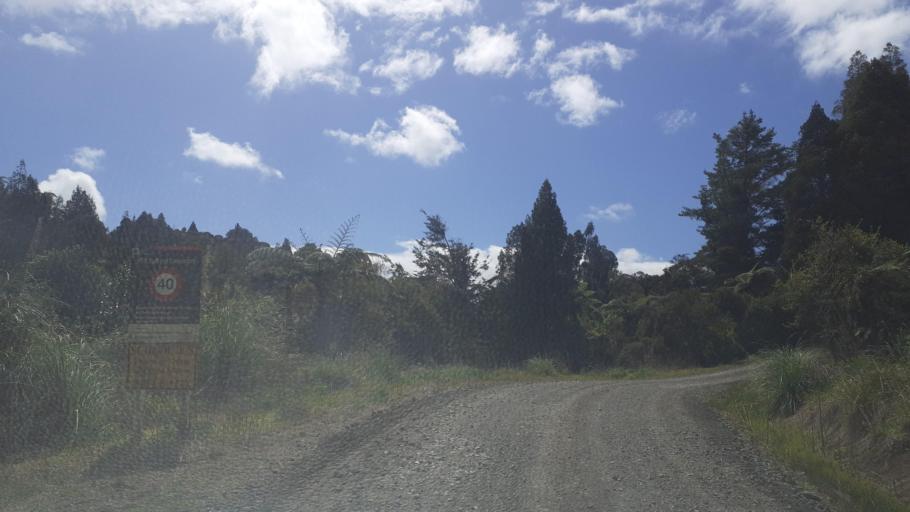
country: NZ
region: Northland
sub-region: Far North District
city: Moerewa
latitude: -35.5840
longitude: 173.9377
